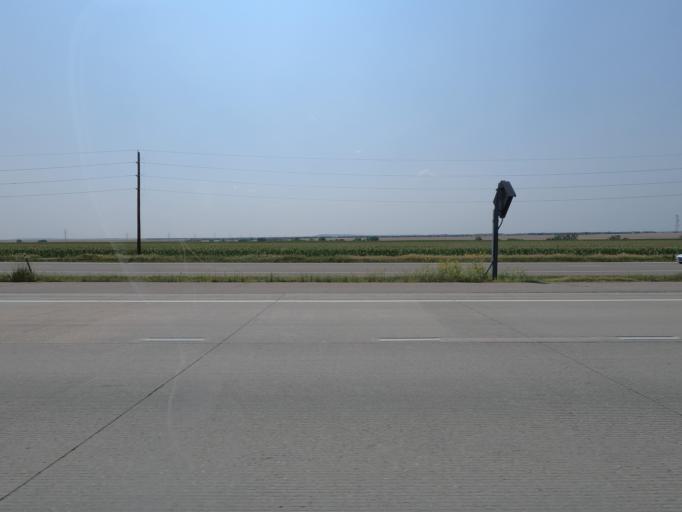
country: US
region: Colorado
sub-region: Adams County
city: Aurora
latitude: 39.7405
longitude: -104.6879
